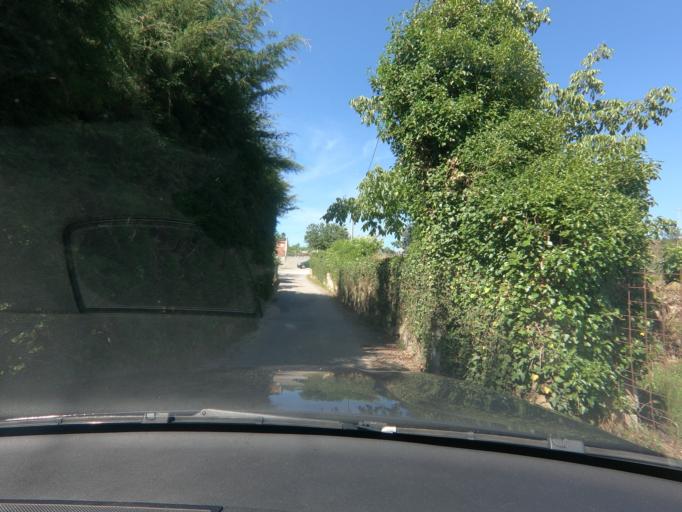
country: PT
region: Vila Real
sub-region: Vila Real
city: Vila Real
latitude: 41.2847
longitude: -7.6941
